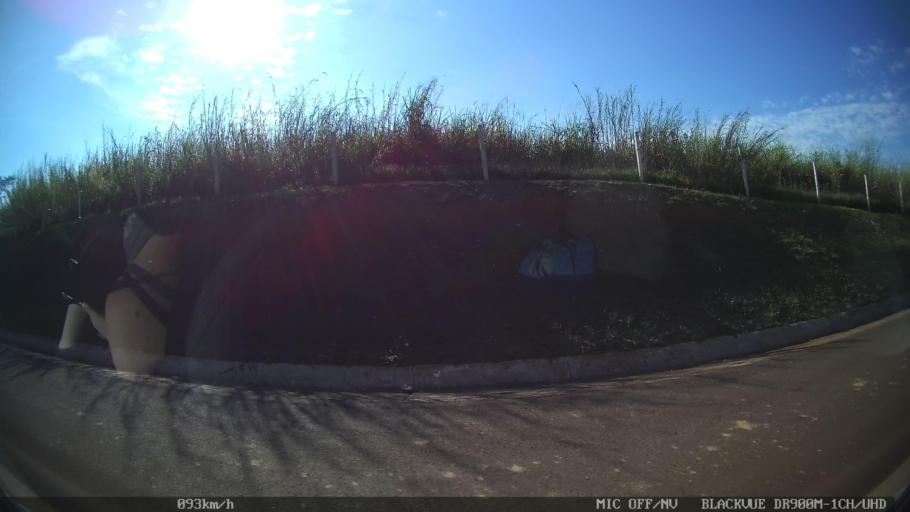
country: BR
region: Sao Paulo
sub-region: Piracicaba
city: Piracicaba
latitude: -22.6822
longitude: -47.5742
